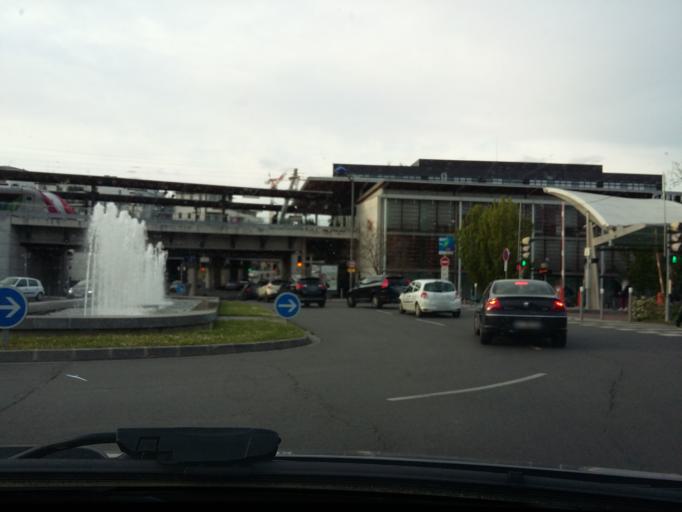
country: FR
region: Ile-de-France
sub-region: Departement du Val-d'Oise
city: Ermont
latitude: 48.9797
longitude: 2.2704
